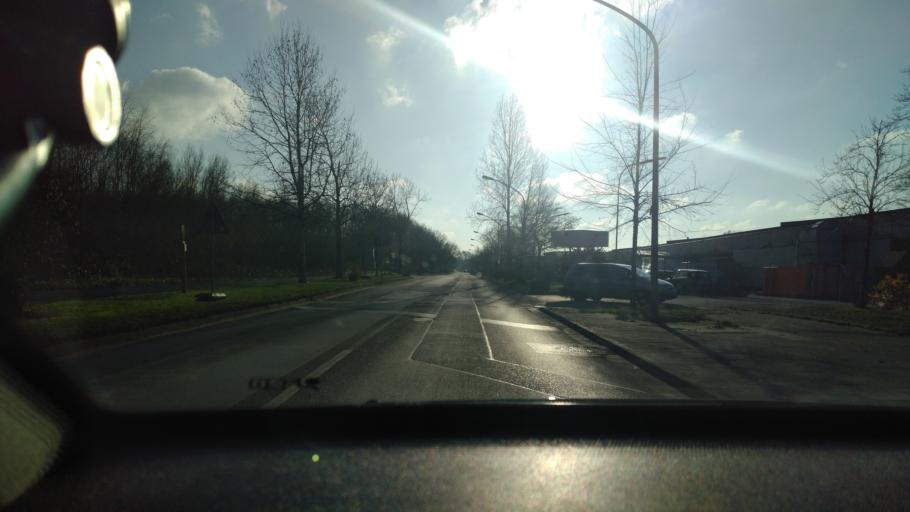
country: DE
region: North Rhine-Westphalia
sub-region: Regierungsbezirk Dusseldorf
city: Essen
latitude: 51.4991
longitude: 6.9802
